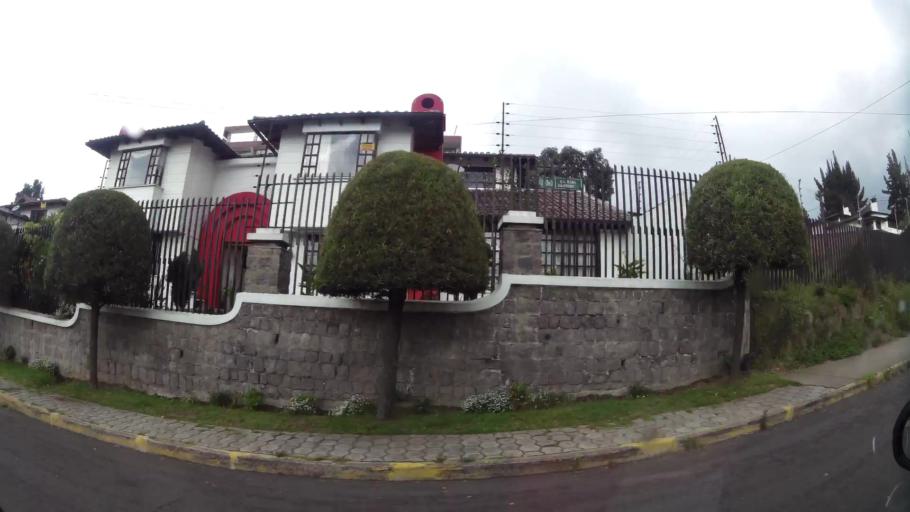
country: EC
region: Pichincha
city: Quito
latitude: -0.0964
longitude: -78.4815
